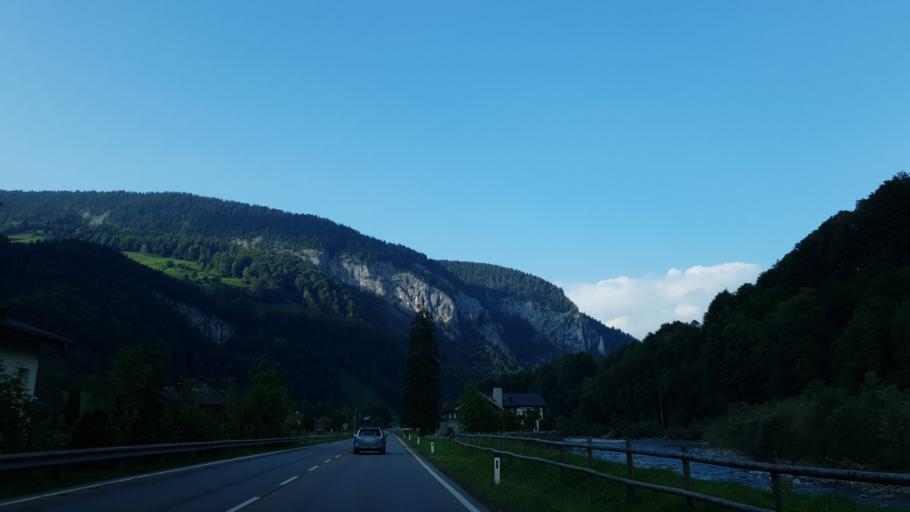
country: AT
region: Vorarlberg
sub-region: Politischer Bezirk Bregenz
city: Reuthe
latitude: 47.3561
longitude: 9.8802
